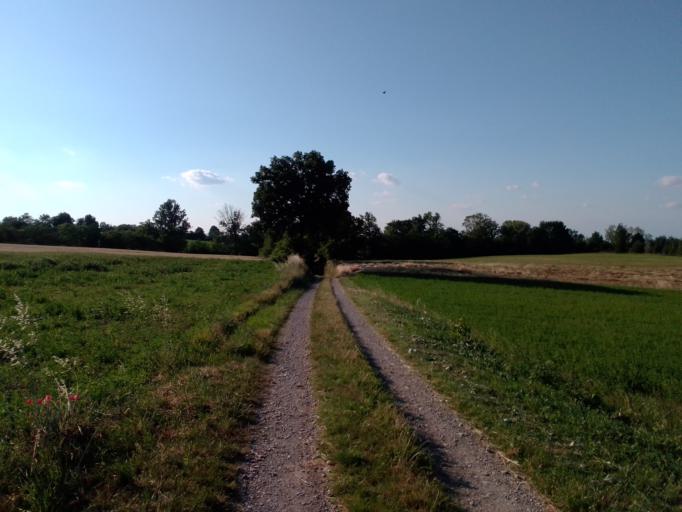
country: IT
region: Emilia-Romagna
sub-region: Provincia di Piacenza
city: Borgonovo Valtidone
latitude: 45.0016
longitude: 9.4348
